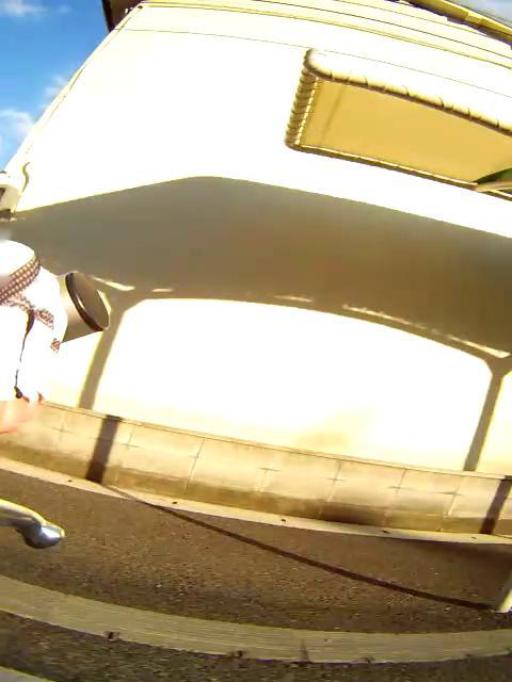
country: JP
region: Hyogo
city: Itami
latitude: 34.7593
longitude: 135.4118
